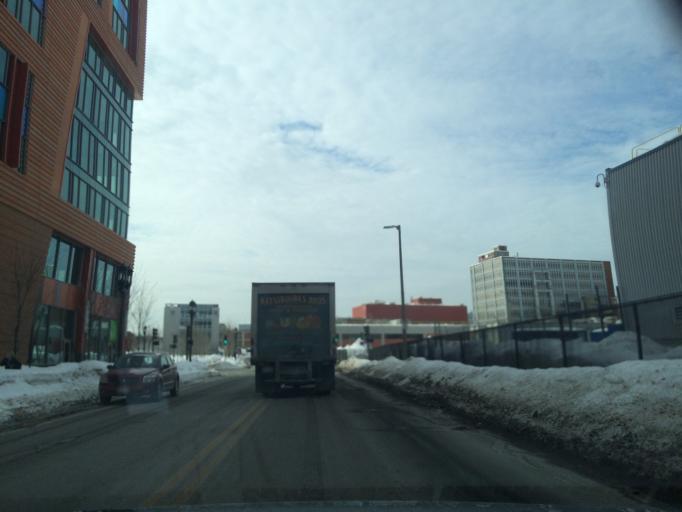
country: US
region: Massachusetts
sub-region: Suffolk County
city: South Boston
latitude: 42.3451
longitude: -71.0527
